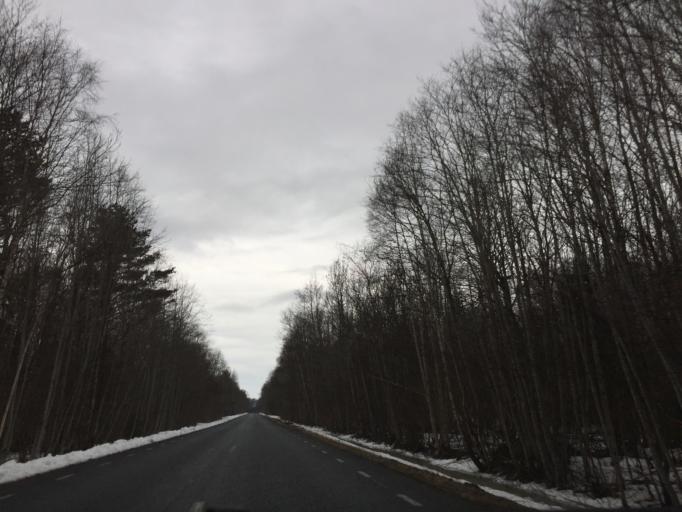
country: EE
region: Saare
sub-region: Orissaare vald
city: Orissaare
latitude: 58.5627
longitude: 22.7705
